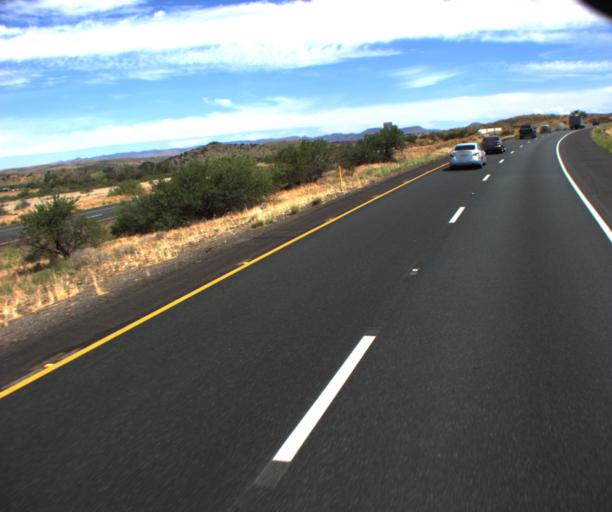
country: US
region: Arizona
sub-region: Yavapai County
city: Cordes Lakes
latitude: 34.4104
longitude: -112.0701
